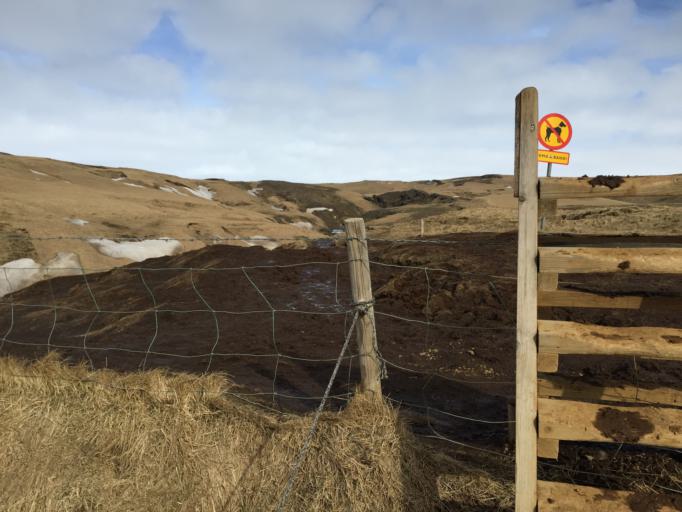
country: IS
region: South
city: Vestmannaeyjar
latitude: 63.5319
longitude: -19.5104
